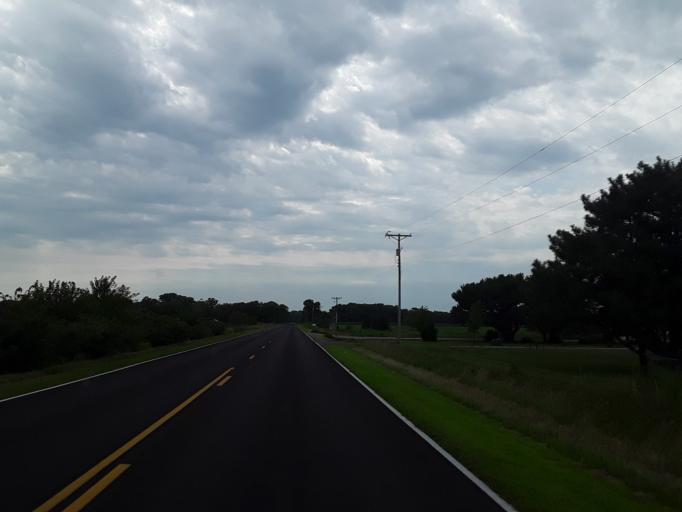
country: US
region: Nebraska
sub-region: Saunders County
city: Yutan
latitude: 41.2192
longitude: -96.3327
